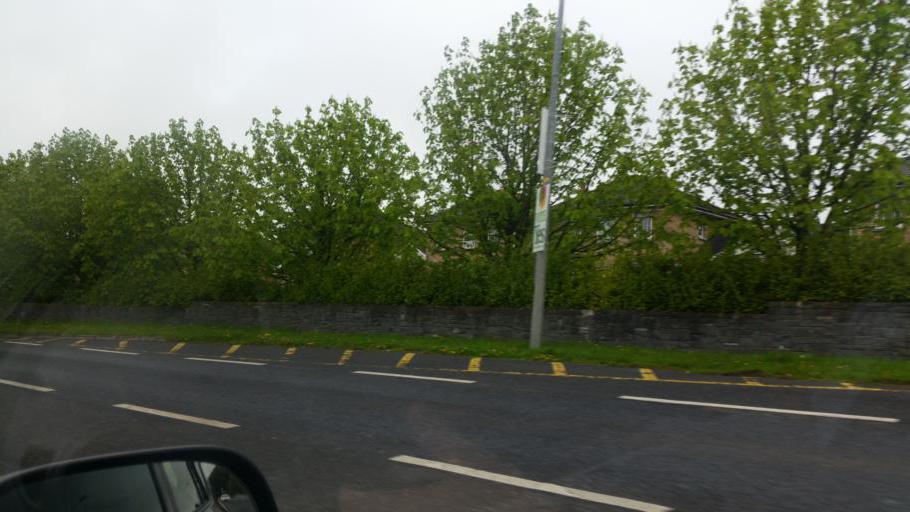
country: IE
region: Leinster
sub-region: Laois
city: Portlaoise
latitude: 53.0433
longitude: -7.2624
